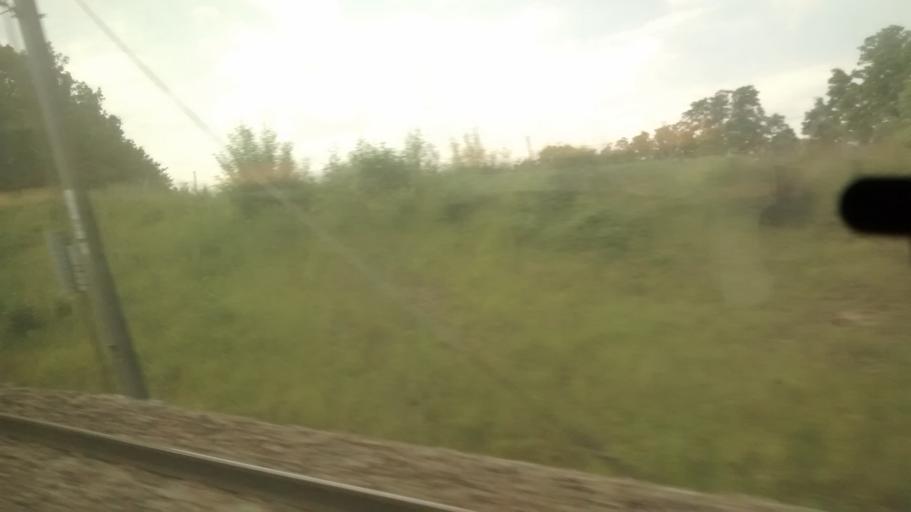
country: FR
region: Bourgogne
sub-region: Departement de Saone-et-Loire
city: Saint-Gengoux-le-National
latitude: 46.5691
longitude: 4.6220
